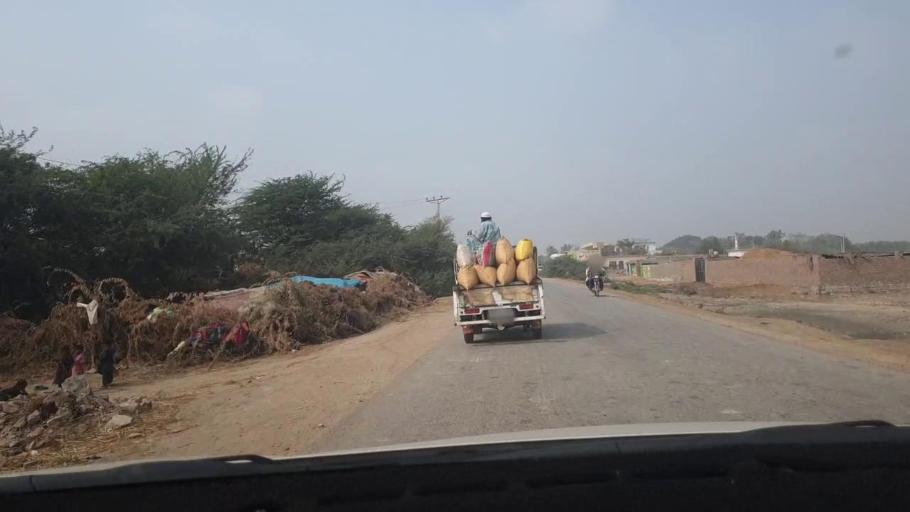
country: PK
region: Sindh
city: Tando Muhammad Khan
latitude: 25.1126
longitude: 68.5340
